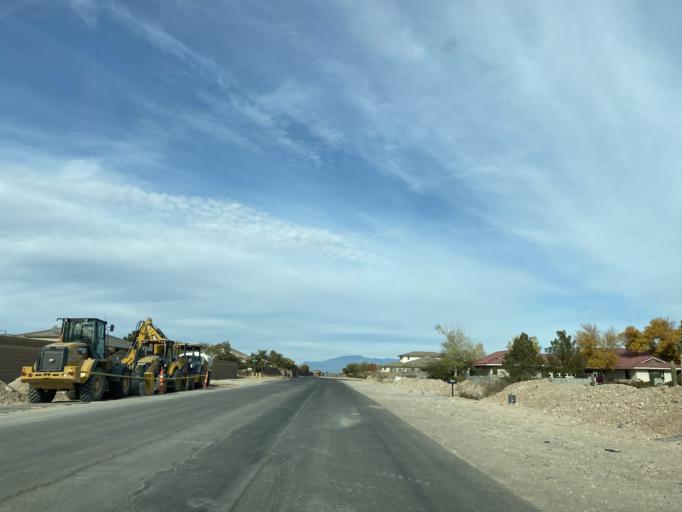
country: US
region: Nevada
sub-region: Clark County
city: Enterprise
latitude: 36.0344
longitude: -115.2699
